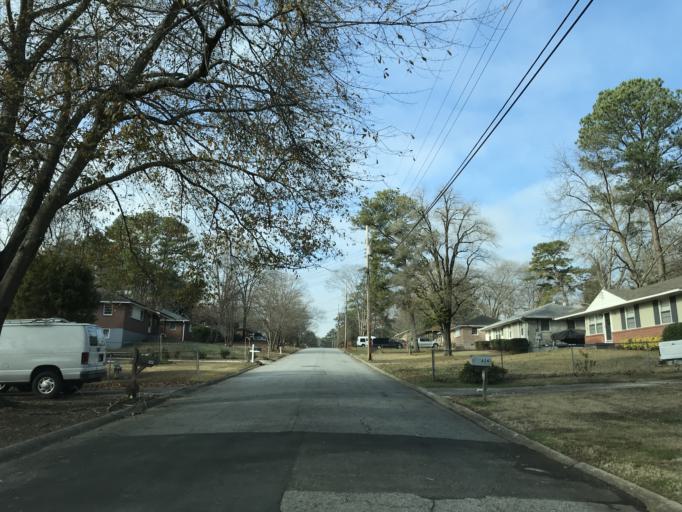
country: US
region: Georgia
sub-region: Clayton County
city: Morrow
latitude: 33.5569
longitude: -84.3645
